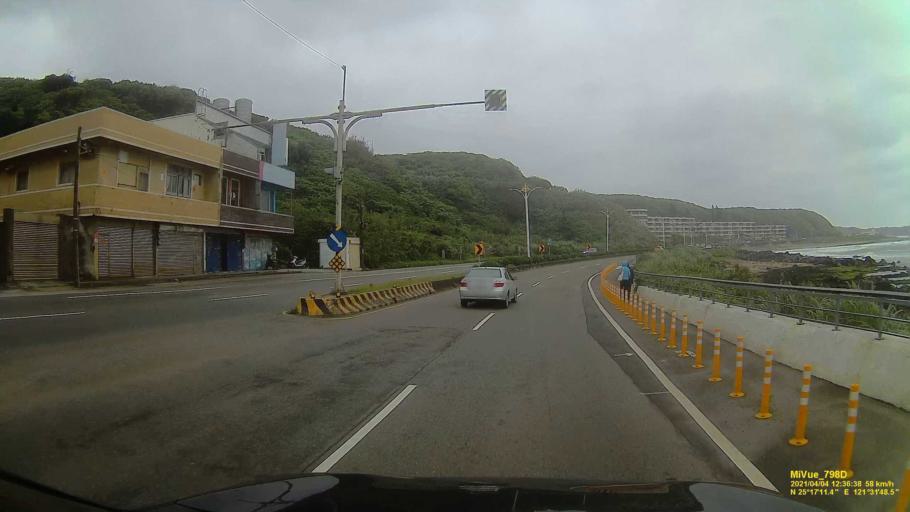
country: TW
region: Taipei
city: Taipei
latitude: 25.2863
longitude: 121.5299
